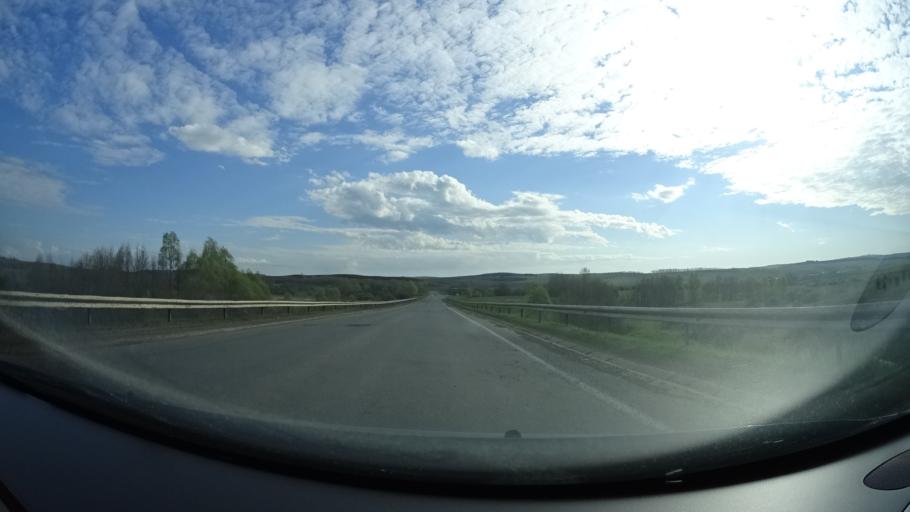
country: RU
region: Bashkortostan
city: Blagoveshchensk
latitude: 55.1062
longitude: 55.8291
